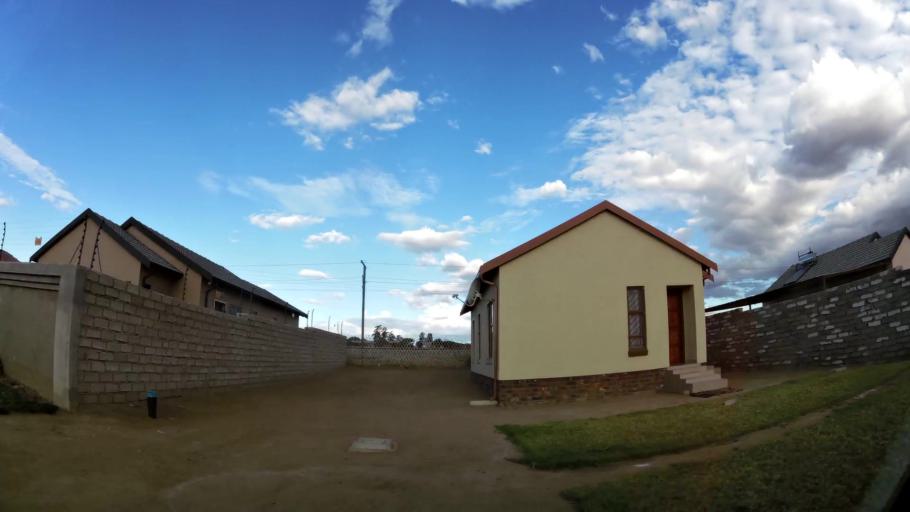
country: ZA
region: Limpopo
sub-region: Capricorn District Municipality
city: Polokwane
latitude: -23.9300
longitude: 29.4146
